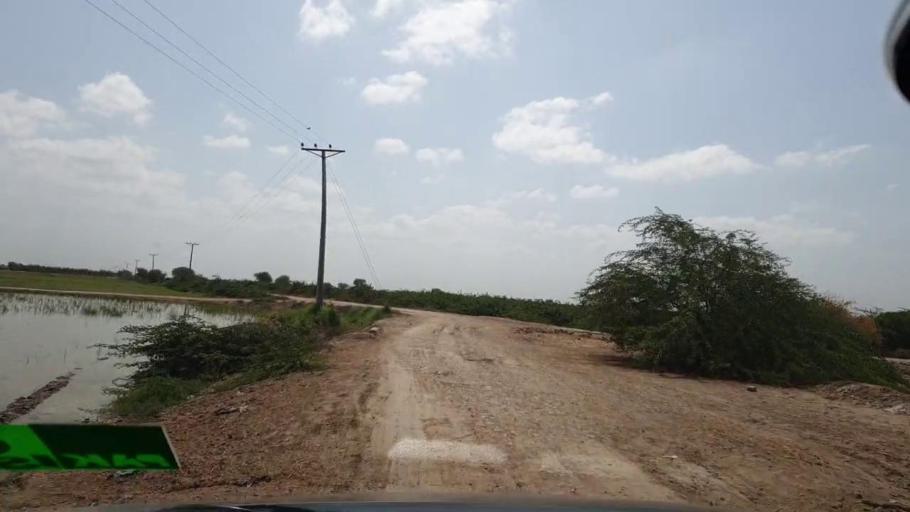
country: PK
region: Sindh
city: Kadhan
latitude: 24.6137
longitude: 69.1855
